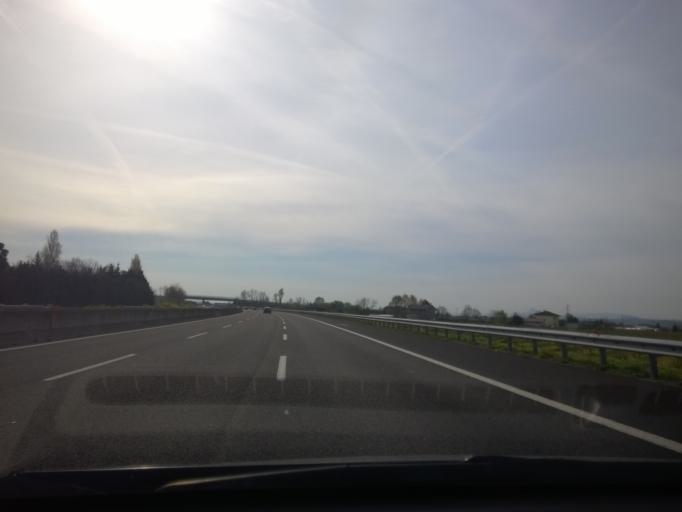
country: IT
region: Emilia-Romagna
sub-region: Forli-Cesena
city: Bagnarola
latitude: 44.1480
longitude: 12.3243
